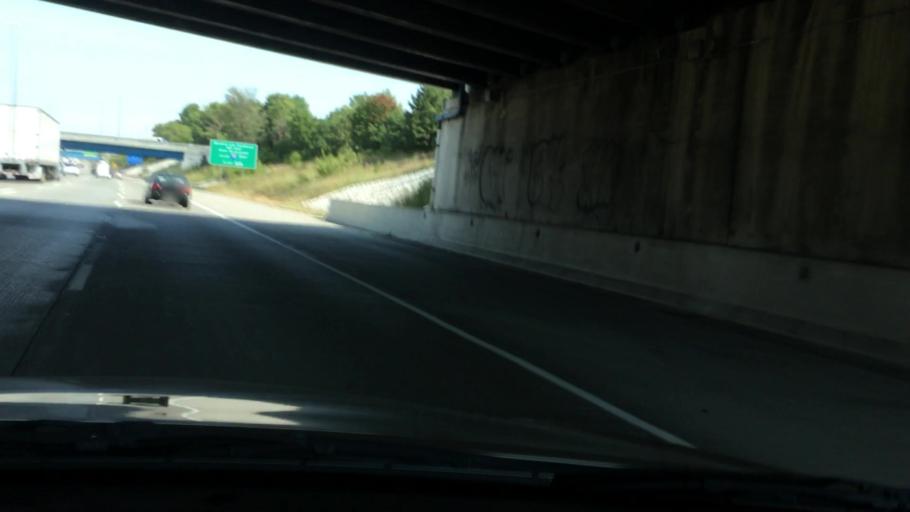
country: US
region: Indiana
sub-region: Marion County
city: Indianapolis
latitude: 39.7577
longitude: -86.1431
